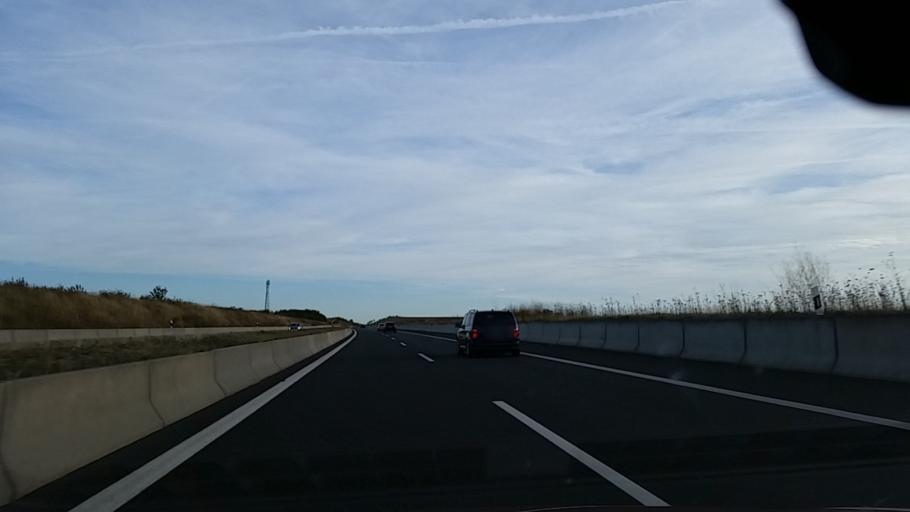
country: DE
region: Bavaria
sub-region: Regierungsbezirk Unterfranken
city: Munnerstadt
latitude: 50.2190
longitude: 10.2186
